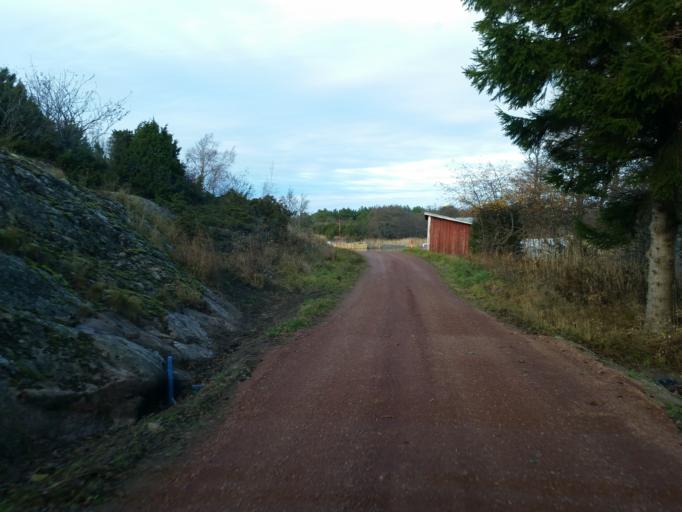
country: AX
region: Alands skaergard
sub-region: Kumlinge
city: Kumlinge
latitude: 60.2519
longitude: 20.7571
